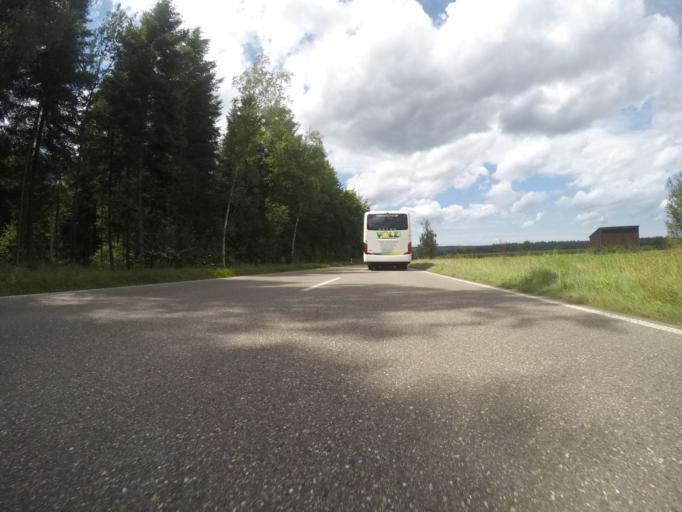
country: DE
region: Baden-Wuerttemberg
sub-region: Karlsruhe Region
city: Calw
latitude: 48.7440
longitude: 8.7593
